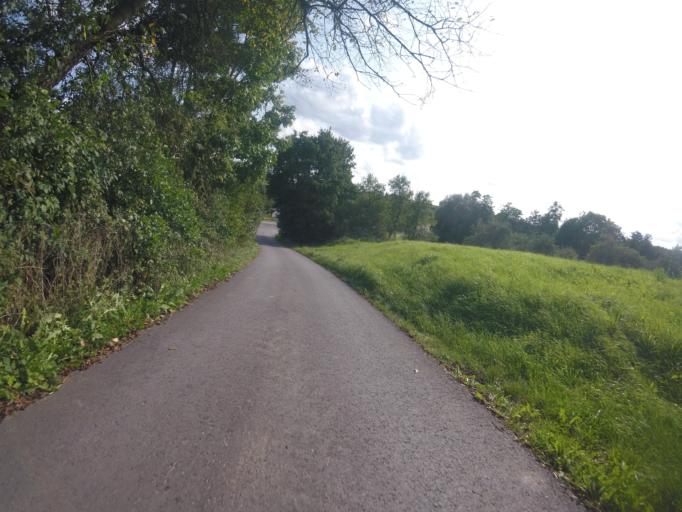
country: DE
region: Baden-Wuerttemberg
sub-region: Regierungsbezirk Stuttgart
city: Aspach
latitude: 48.9928
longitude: 9.4063
